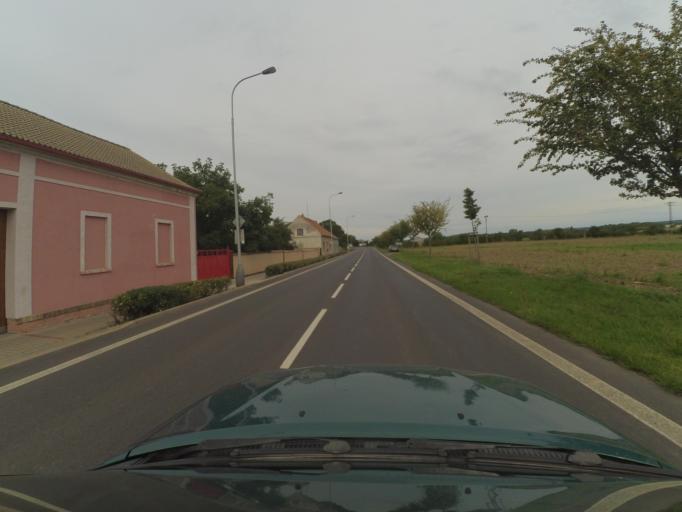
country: CZ
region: Ustecky
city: Cerncice
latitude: 50.3638
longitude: 13.8508
